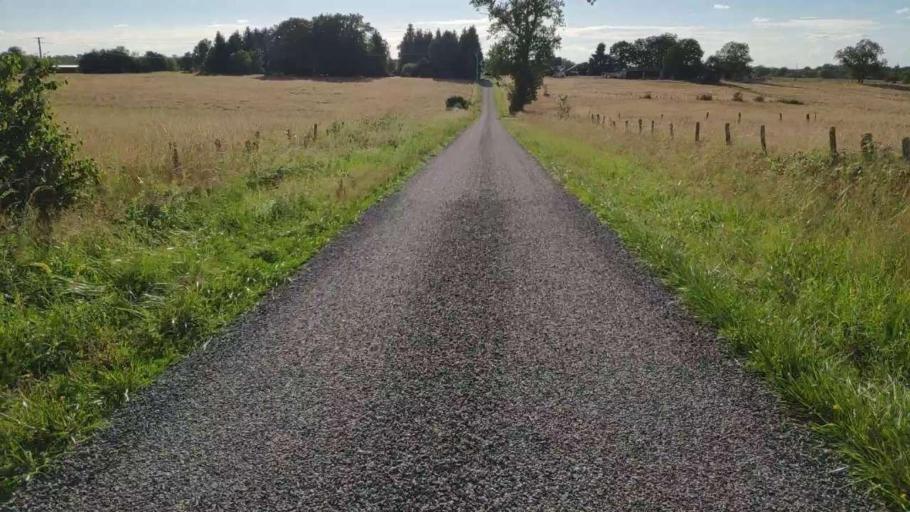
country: FR
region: Franche-Comte
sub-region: Departement du Jura
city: Bletterans
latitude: 46.8000
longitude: 5.4856
